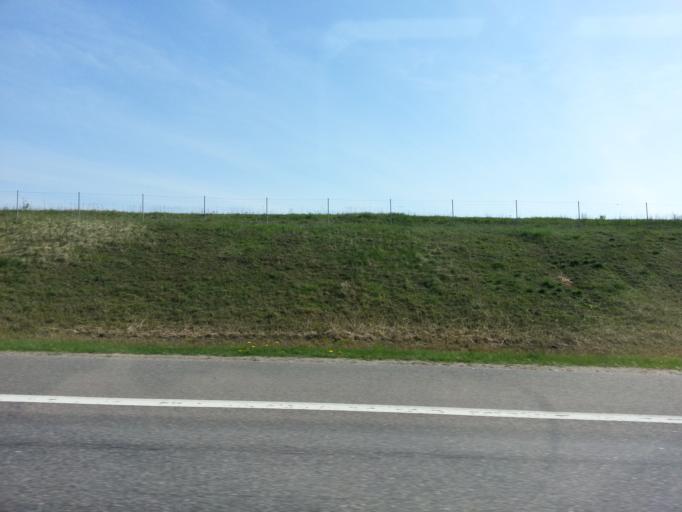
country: LT
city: Grigiskes
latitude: 54.8828
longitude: 25.0650
